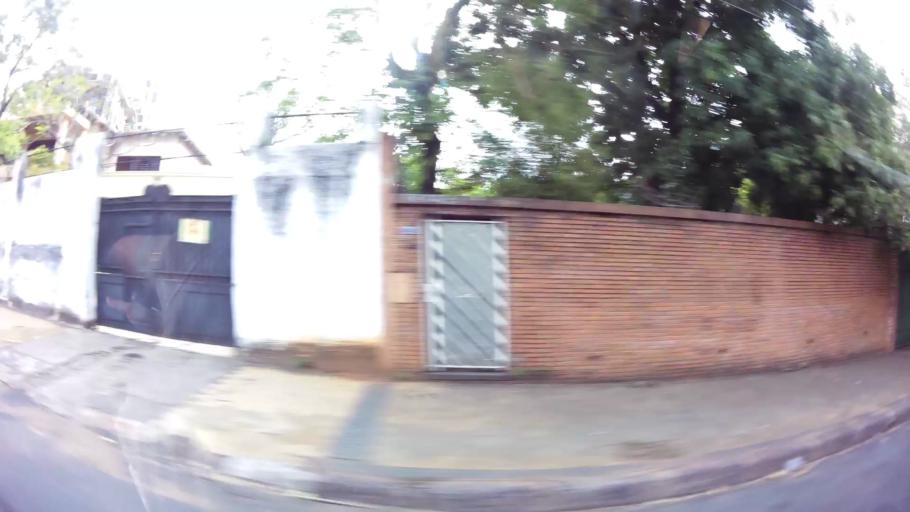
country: PY
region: Asuncion
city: Asuncion
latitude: -25.2919
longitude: -57.6107
